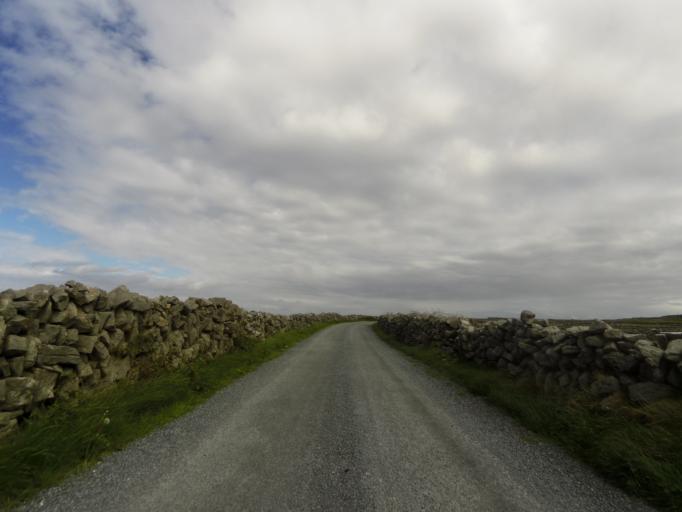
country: IE
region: Connaught
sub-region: County Galway
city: Clifden
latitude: 53.1329
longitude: -9.7455
